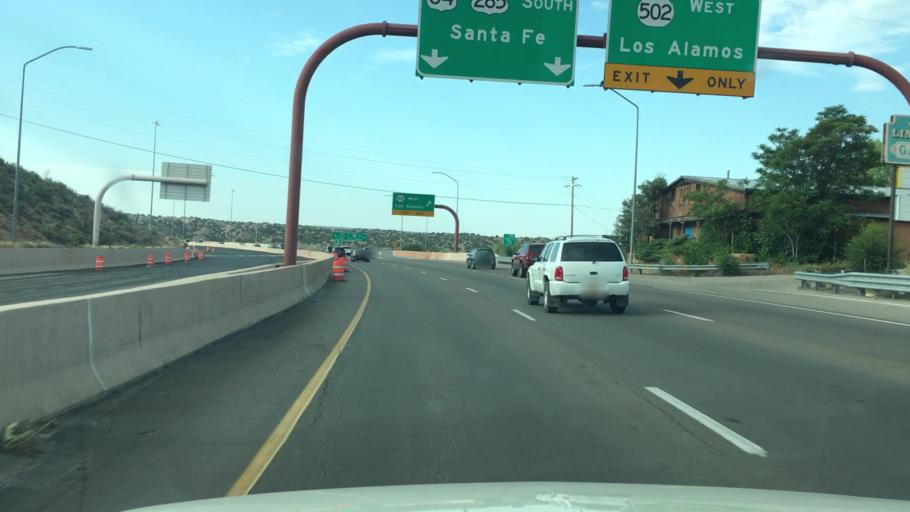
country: US
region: New Mexico
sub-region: Santa Fe County
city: Pojoaque
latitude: 35.8941
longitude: -106.0228
